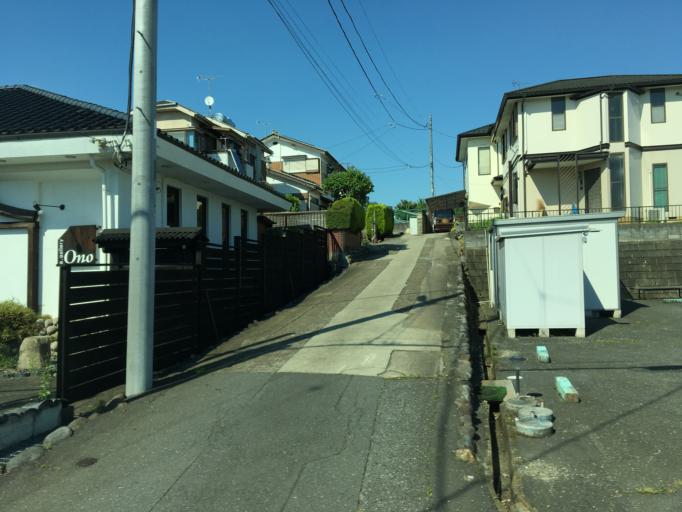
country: JP
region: Saitama
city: Morohongo
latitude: 35.9750
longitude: 139.3381
